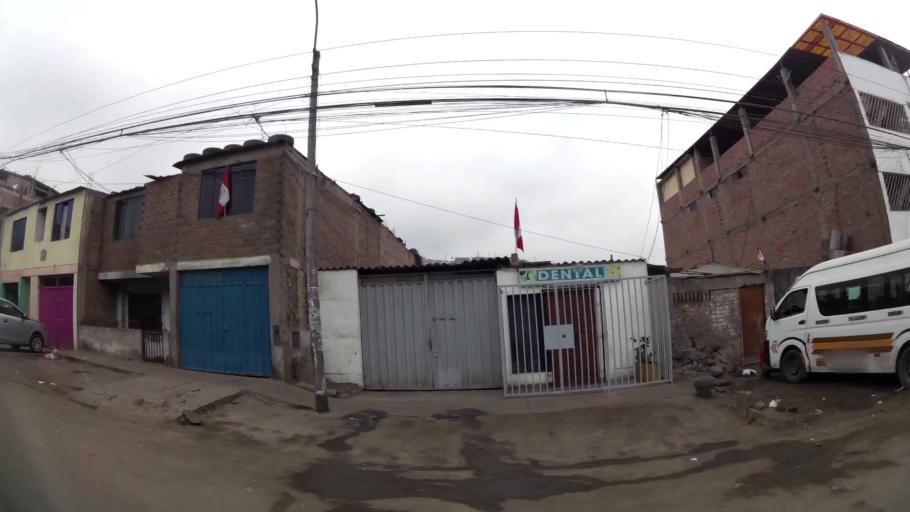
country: PE
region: Lima
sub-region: Lima
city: Surco
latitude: -12.1345
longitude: -76.9581
